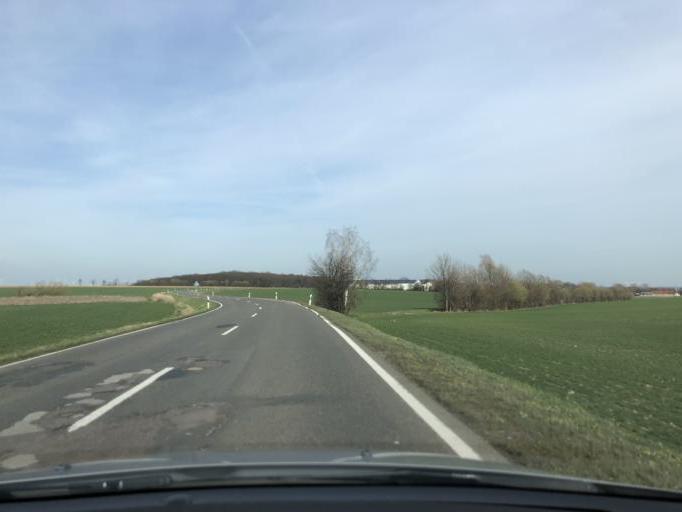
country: DE
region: Saxony-Anhalt
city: Osterfeld
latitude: 51.0681
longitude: 11.9759
